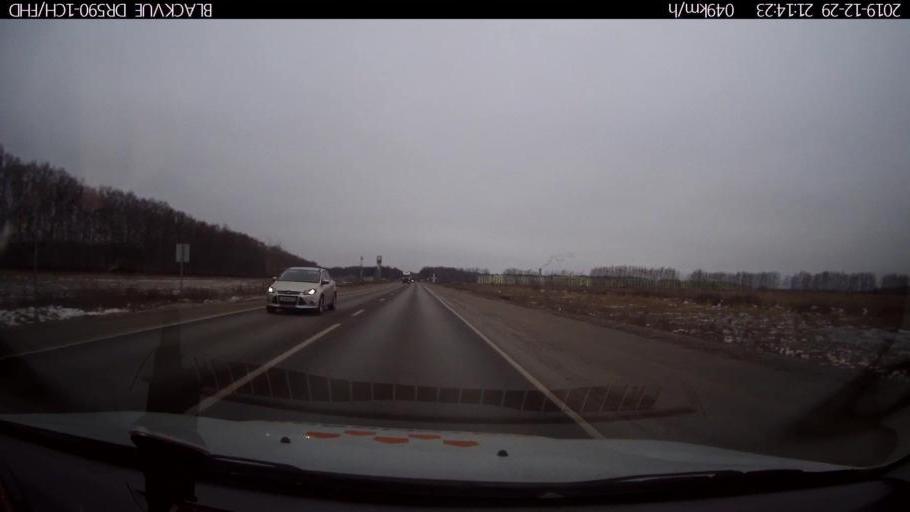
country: RU
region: Nizjnij Novgorod
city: Afonino
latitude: 56.2142
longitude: 44.0318
